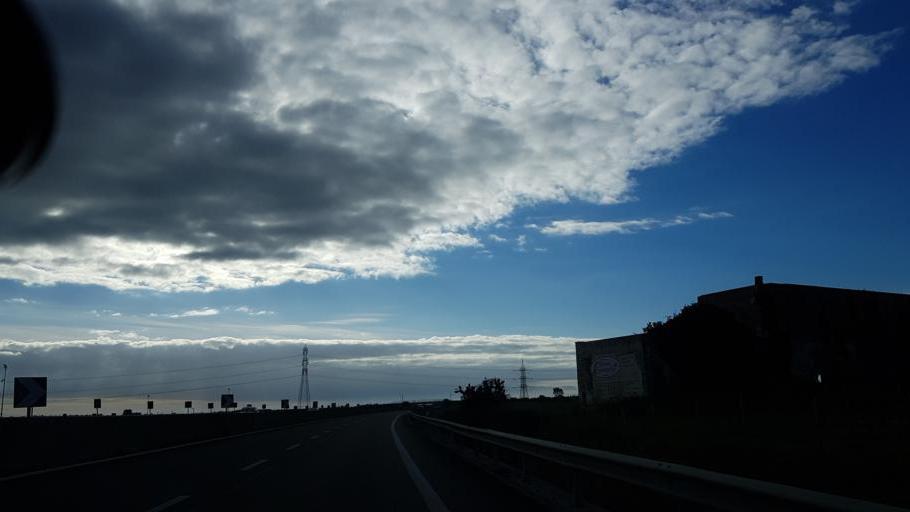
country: IT
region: Apulia
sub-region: Provincia di Brindisi
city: La Rosa
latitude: 40.6069
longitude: 17.9636
